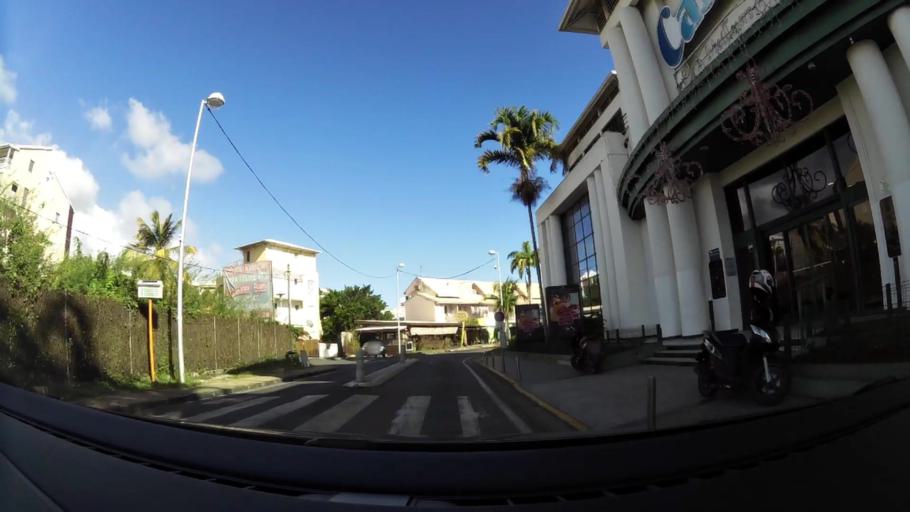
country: GP
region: Guadeloupe
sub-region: Guadeloupe
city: Le Gosier
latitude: 16.2079
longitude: -61.5038
